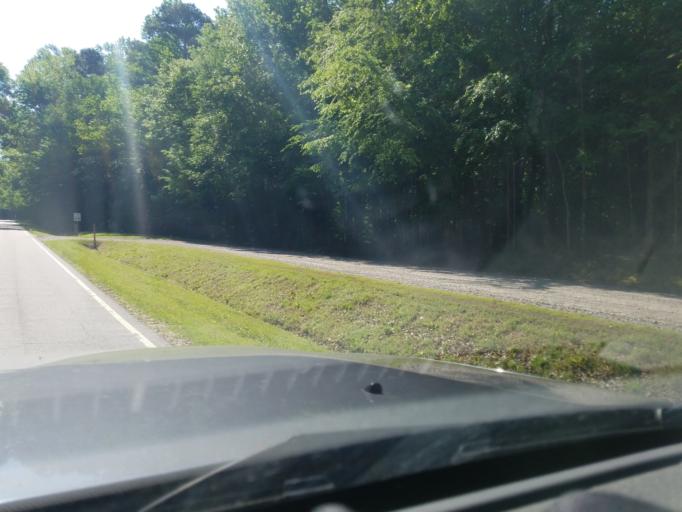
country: US
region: North Carolina
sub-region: Vance County
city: Henderson
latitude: 36.4084
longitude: -78.3896
